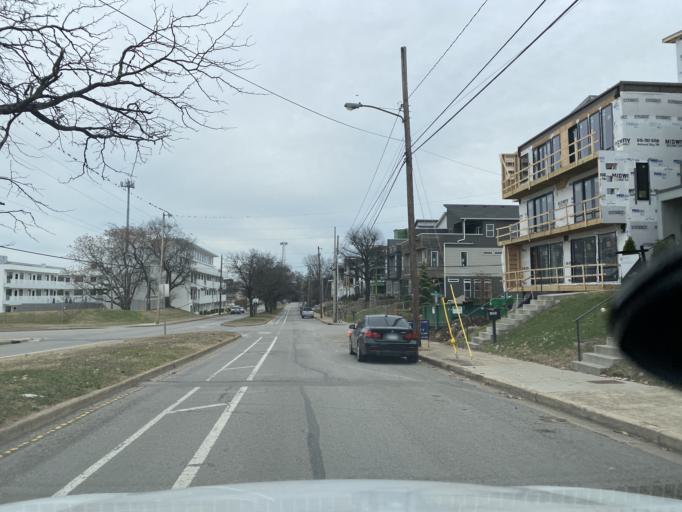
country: US
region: Tennessee
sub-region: Davidson County
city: Nashville
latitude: 36.1470
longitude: -86.7830
